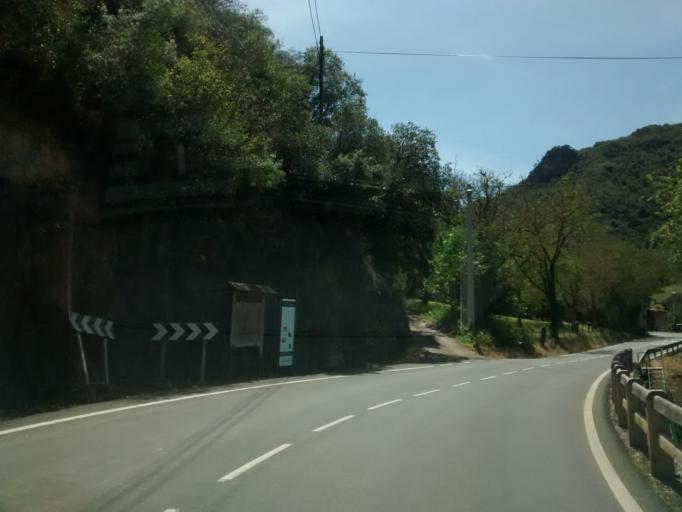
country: ES
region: Cantabria
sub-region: Provincia de Cantabria
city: Potes
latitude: 43.1333
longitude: -4.6301
